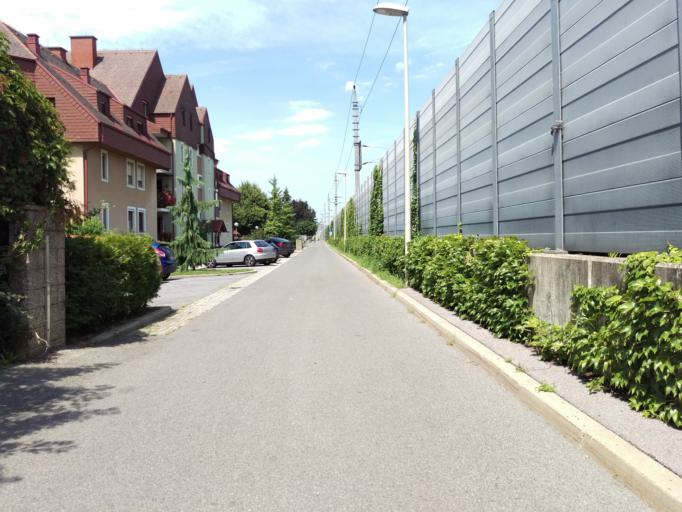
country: AT
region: Styria
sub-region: Politischer Bezirk Graz-Umgebung
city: Feldkirchen bei Graz
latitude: 47.0230
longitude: 15.4338
